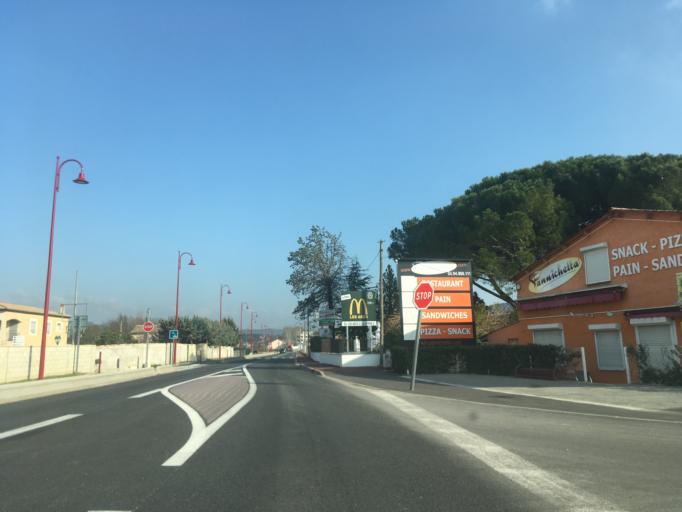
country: FR
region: Provence-Alpes-Cote d'Azur
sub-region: Departement du Var
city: Vidauban
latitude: 43.4197
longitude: 6.4241
